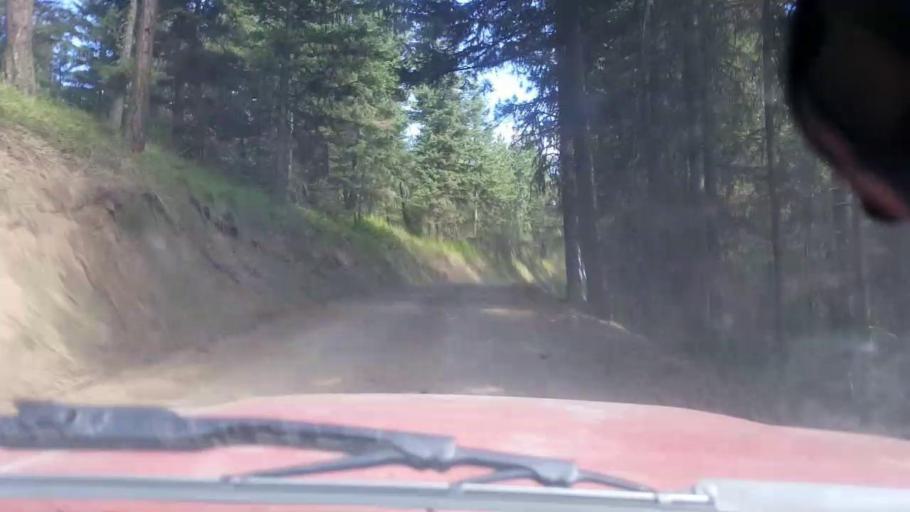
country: US
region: Washington
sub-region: Asotin County
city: Asotin
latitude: 46.0303
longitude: -117.4047
